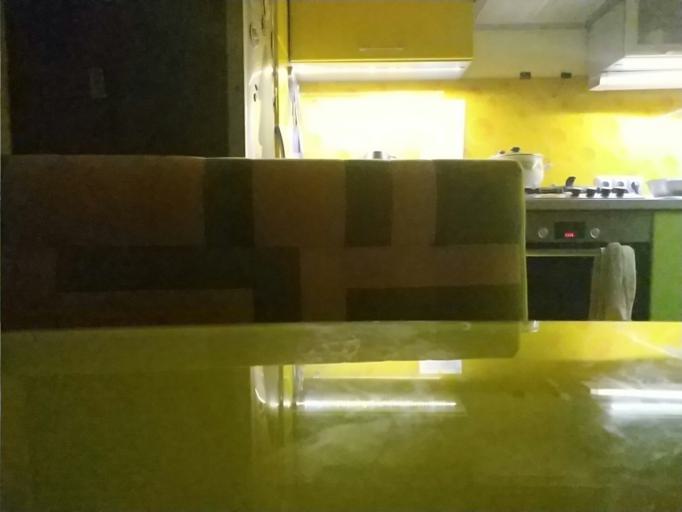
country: RU
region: Republic of Karelia
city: Pyaozerskiy
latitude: 65.9185
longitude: 30.4189
